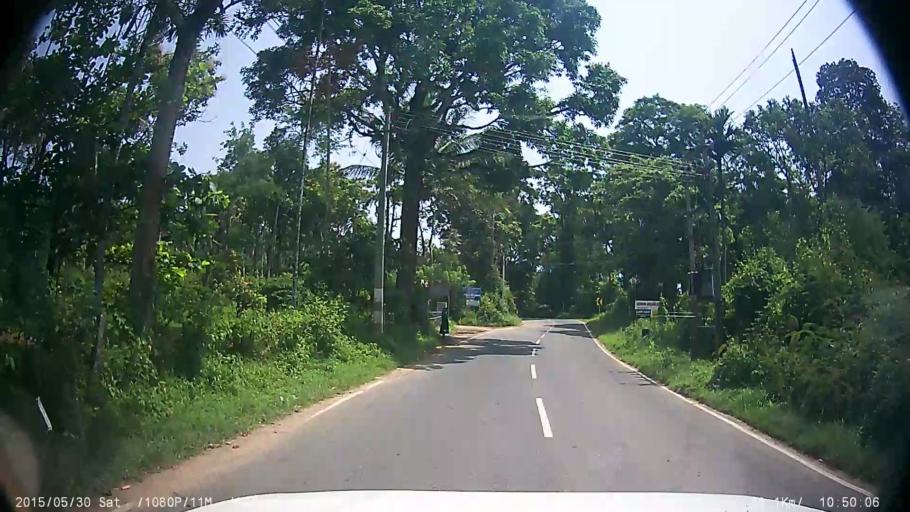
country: IN
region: Kerala
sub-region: Wayanad
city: Kalpetta
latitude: 11.6413
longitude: 76.0869
